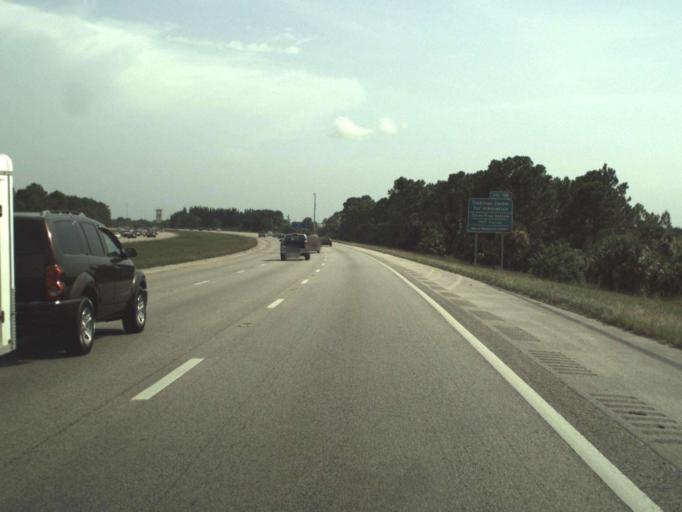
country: US
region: Florida
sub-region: Saint Lucie County
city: Port Saint Lucie
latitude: 27.2860
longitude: -80.4235
